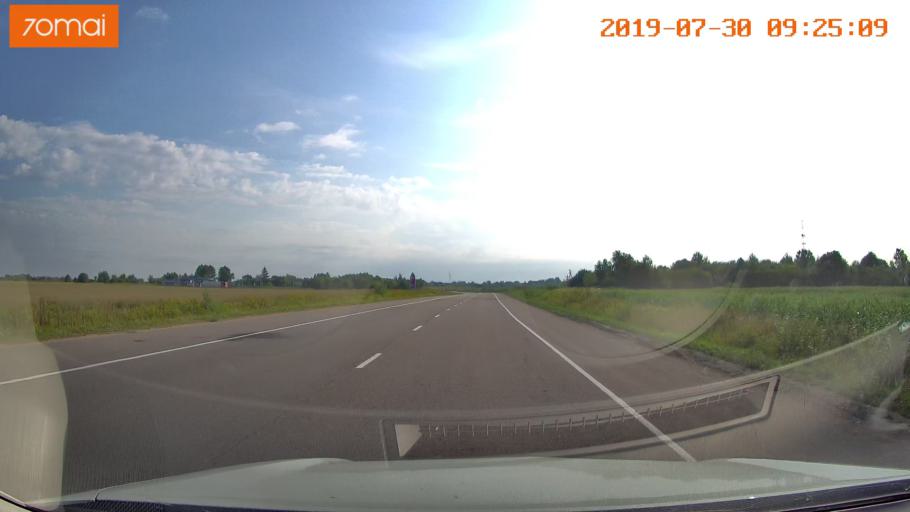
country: LT
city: Kybartai
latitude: 54.6373
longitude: 22.7088
